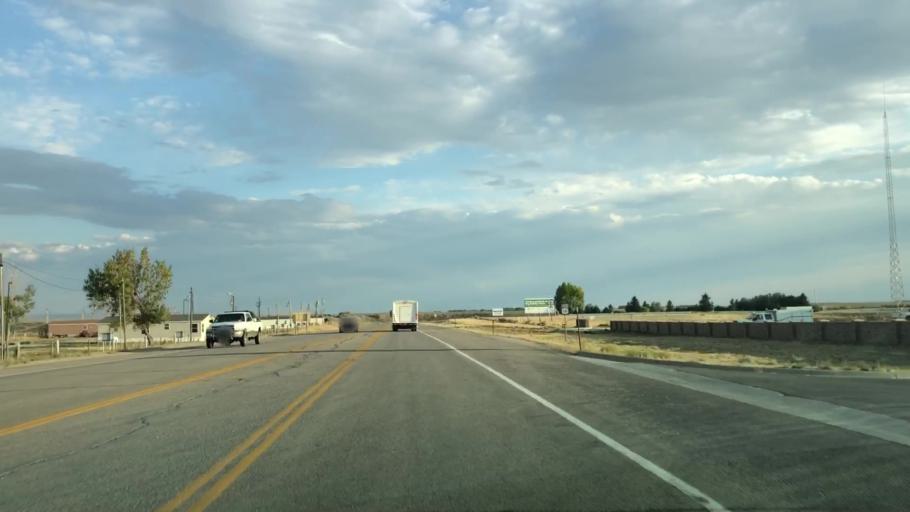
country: US
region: Wyoming
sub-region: Sweetwater County
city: North Rock Springs
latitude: 42.1074
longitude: -109.4487
